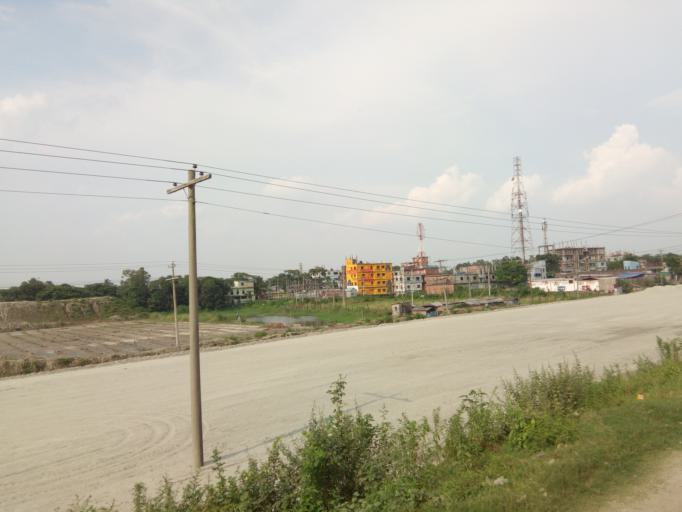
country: BD
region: Dhaka
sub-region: Dhaka
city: Dhaka
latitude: 23.6628
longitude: 90.3857
